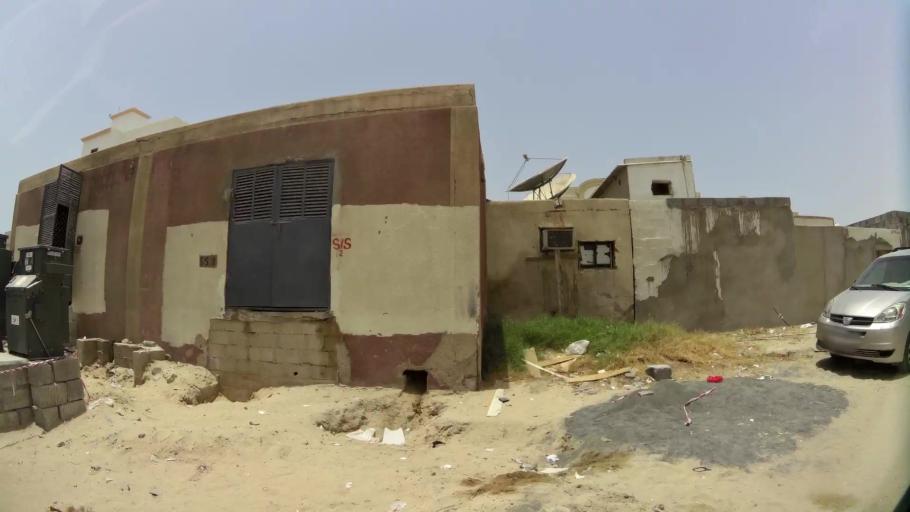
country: AE
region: Ash Shariqah
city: Sharjah
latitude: 25.3556
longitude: 55.3989
